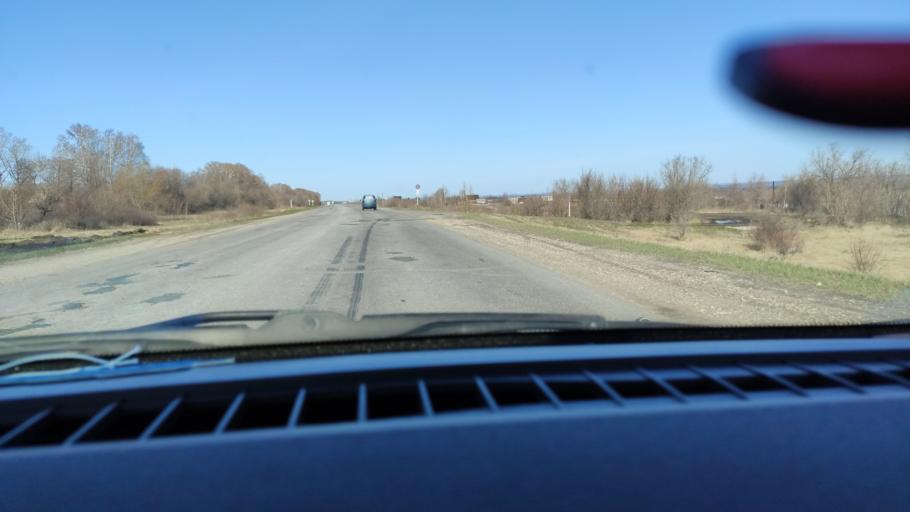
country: RU
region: Samara
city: Varlamovo
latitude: 53.1216
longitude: 48.3202
